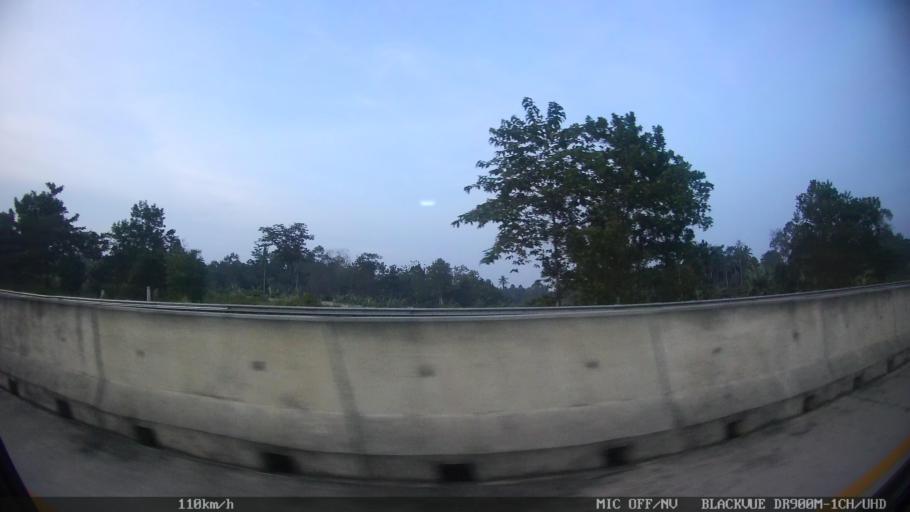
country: ID
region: Lampung
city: Pasuruan
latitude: -5.7330
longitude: 105.6842
